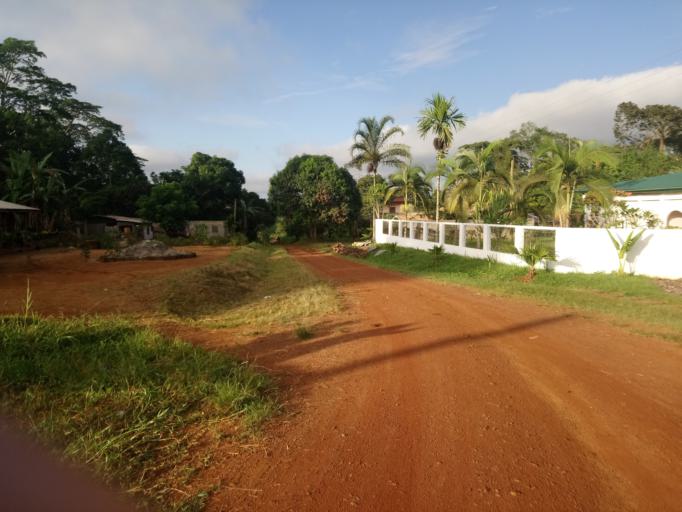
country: CM
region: Centre
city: Akono
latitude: 3.5836
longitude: 11.3381
